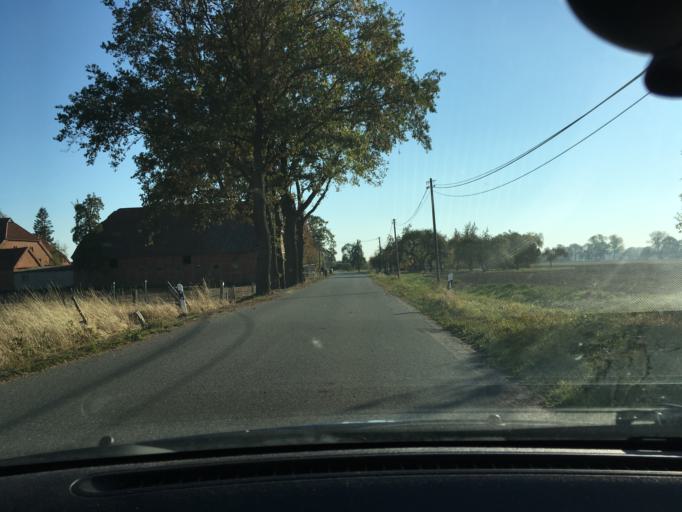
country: DE
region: Lower Saxony
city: Hitzacker
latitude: 53.1606
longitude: 11.1109
